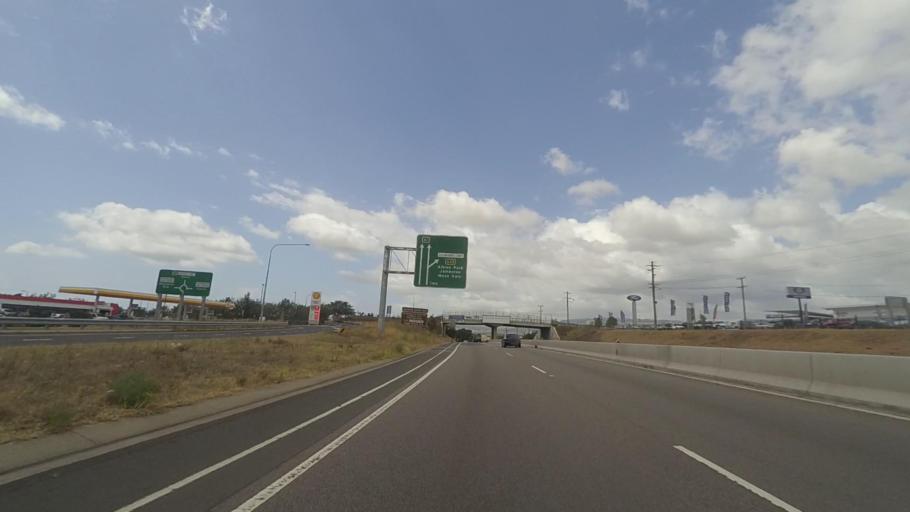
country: AU
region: New South Wales
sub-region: Shellharbour
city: Albion Park Rail
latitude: -34.5405
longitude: 150.7847
